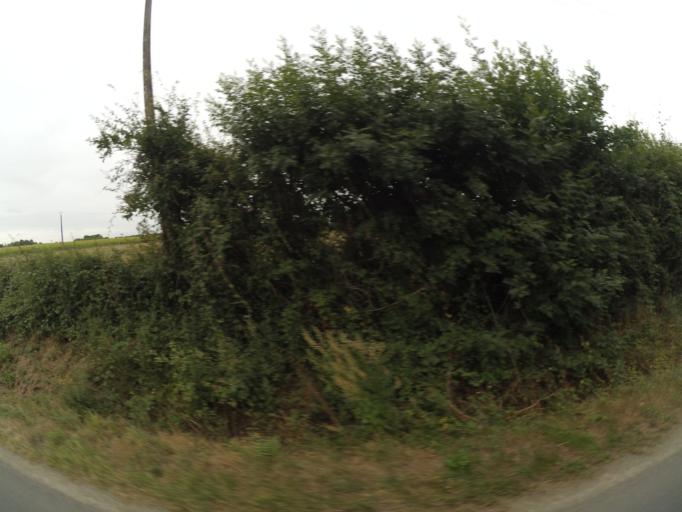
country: FR
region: Pays de la Loire
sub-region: Departement de la Vendee
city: Saint-Andre-Treize-Voies
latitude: 46.9308
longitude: -1.4024
